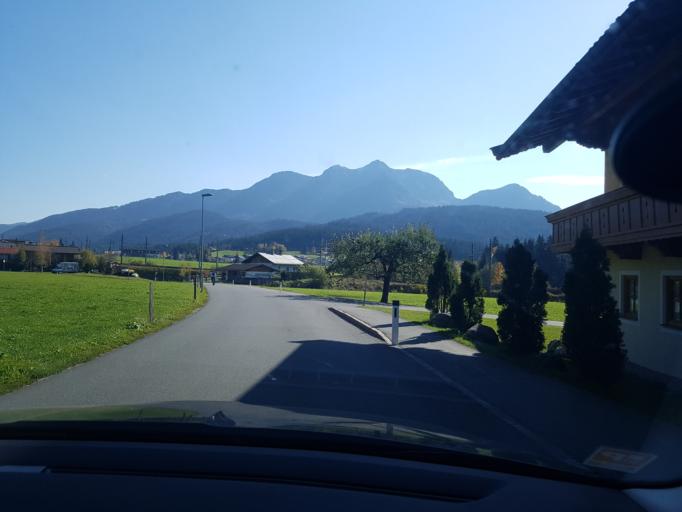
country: AT
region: Tyrol
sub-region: Politischer Bezirk Kitzbuhel
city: Hochfilzen
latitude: 47.4761
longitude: 12.6148
